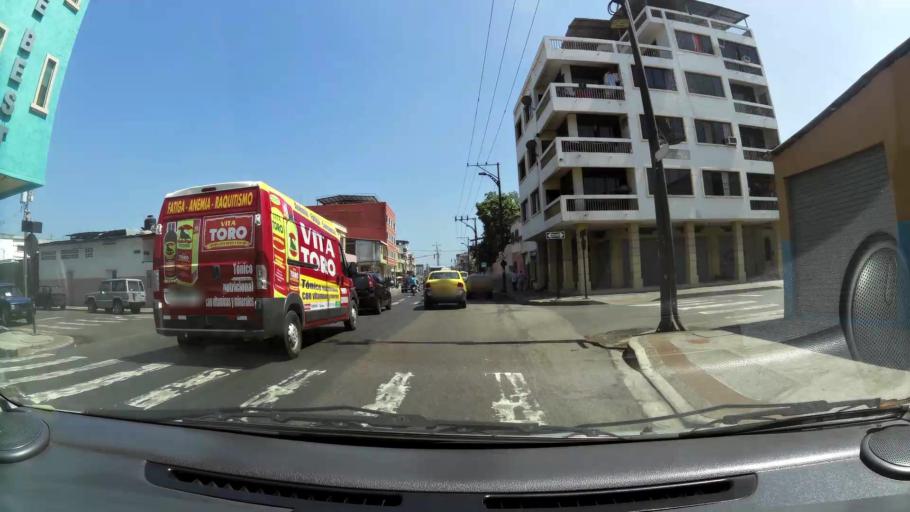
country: EC
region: Guayas
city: Guayaquil
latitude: -2.2033
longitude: -79.9102
